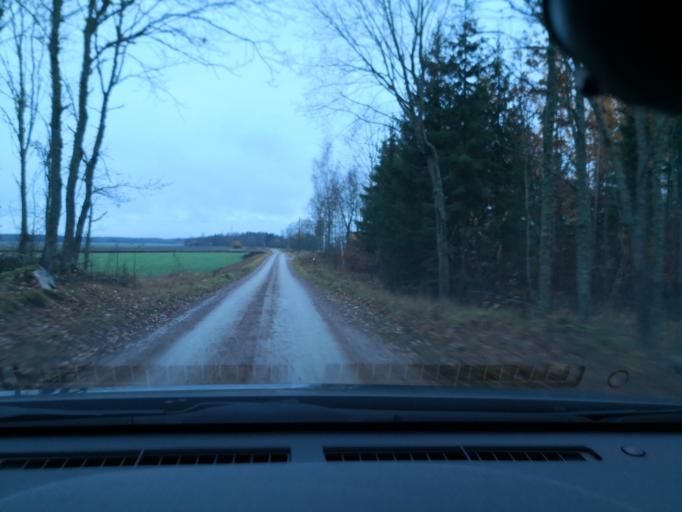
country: SE
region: Vaestmanland
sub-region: Hallstahammars Kommun
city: Kolback
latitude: 59.5558
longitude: 16.1875
